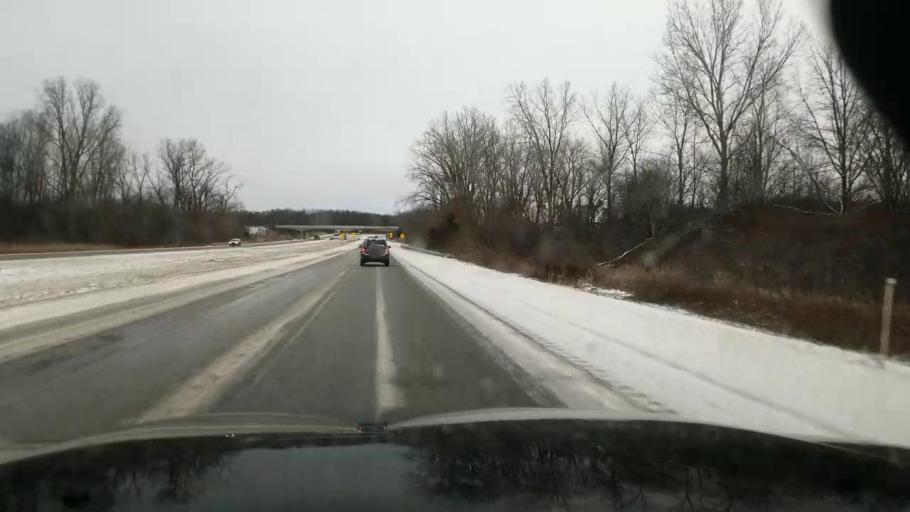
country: US
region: Michigan
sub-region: Jackson County
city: Jackson
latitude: 42.2361
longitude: -84.4754
